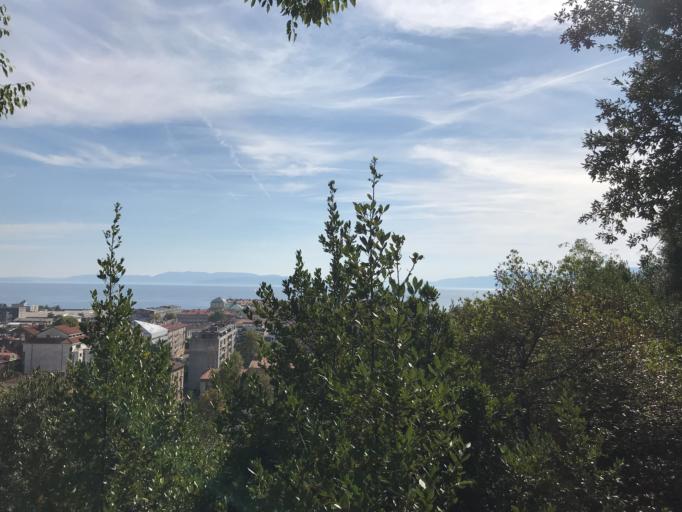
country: HR
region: Primorsko-Goranska
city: Drenova
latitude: 45.3302
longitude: 14.4477
